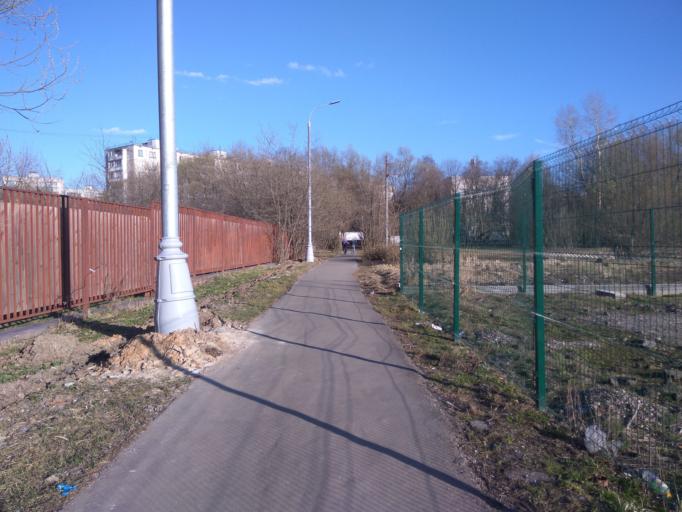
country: RU
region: Moscow
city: Veshnyaki
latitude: 55.7269
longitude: 37.8051
